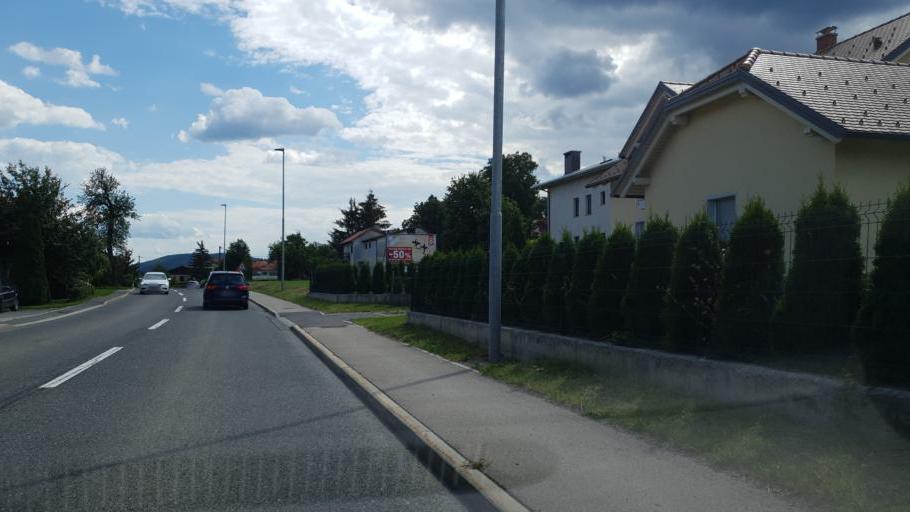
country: SI
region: Postojna
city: Postojna
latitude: 45.7416
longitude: 14.1929
